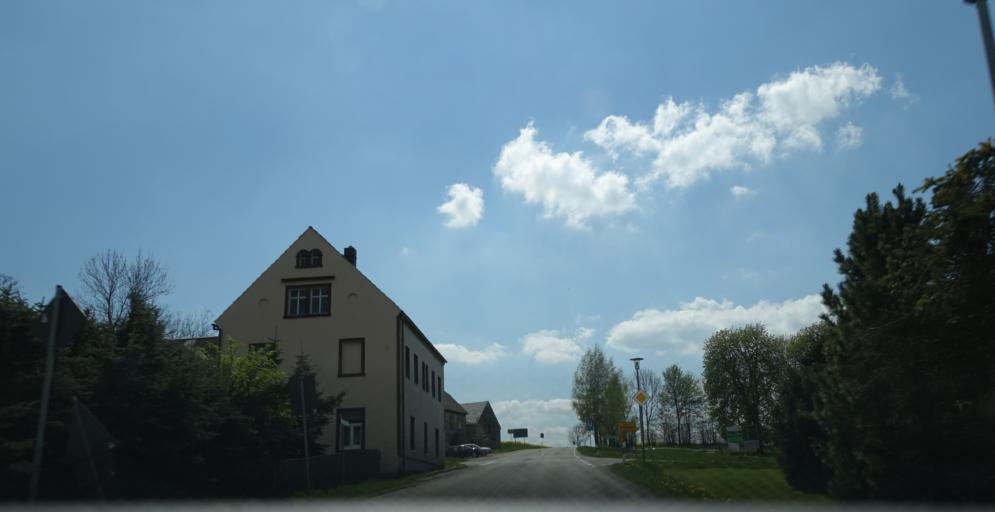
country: DE
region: Saxony
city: Grosshartmannsdorf
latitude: 50.7637
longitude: 13.3112
